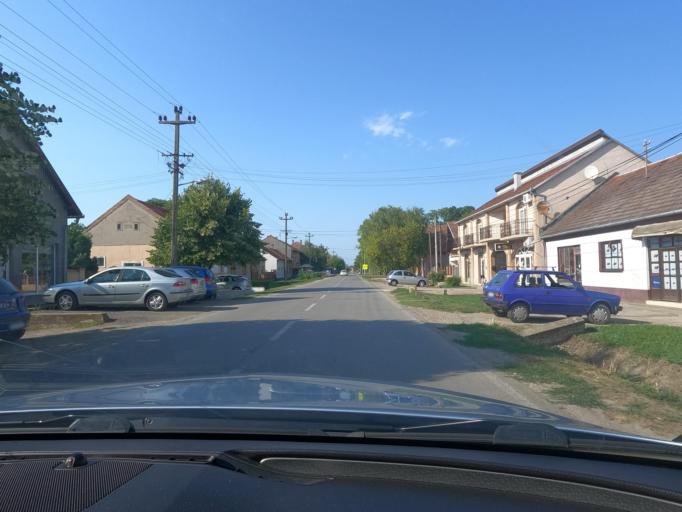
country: RS
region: Autonomna Pokrajina Vojvodina
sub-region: Juznobacki Okrug
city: Kovilj
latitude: 45.2232
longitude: 20.0206
